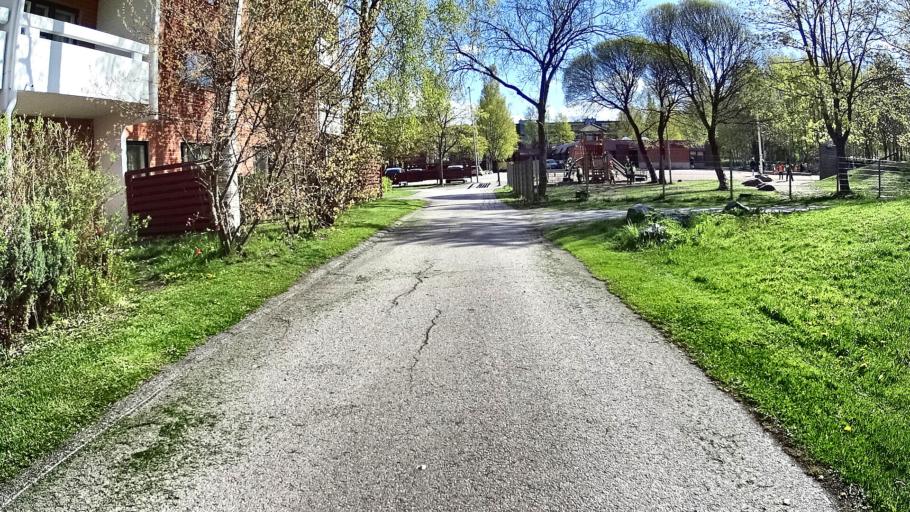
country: FI
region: Uusimaa
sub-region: Helsinki
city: Vantaa
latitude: 60.2056
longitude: 25.0784
